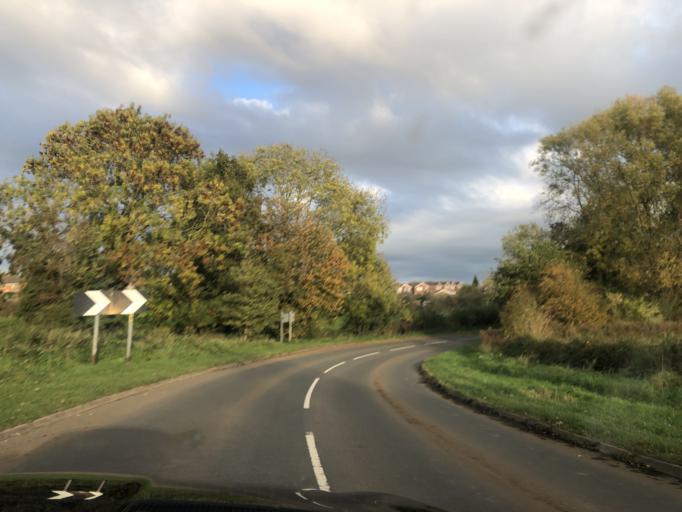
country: GB
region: England
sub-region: Warwickshire
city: Harbury
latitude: 52.2349
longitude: -1.4685
